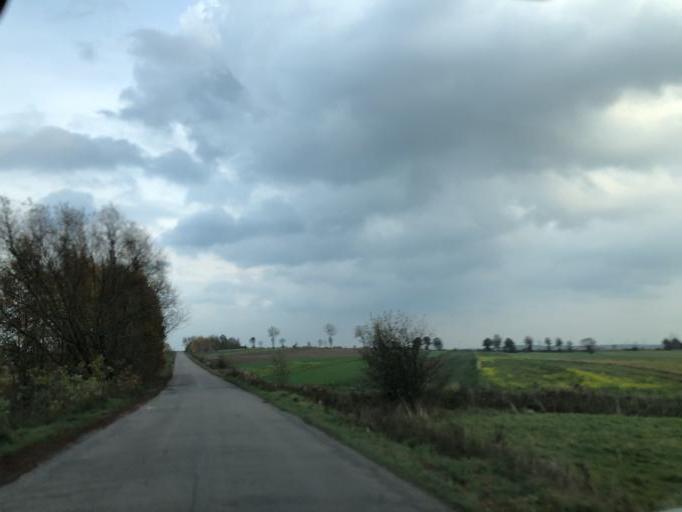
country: PL
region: Podlasie
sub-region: Lomza
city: Lomza
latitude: 53.1180
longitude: 22.0230
